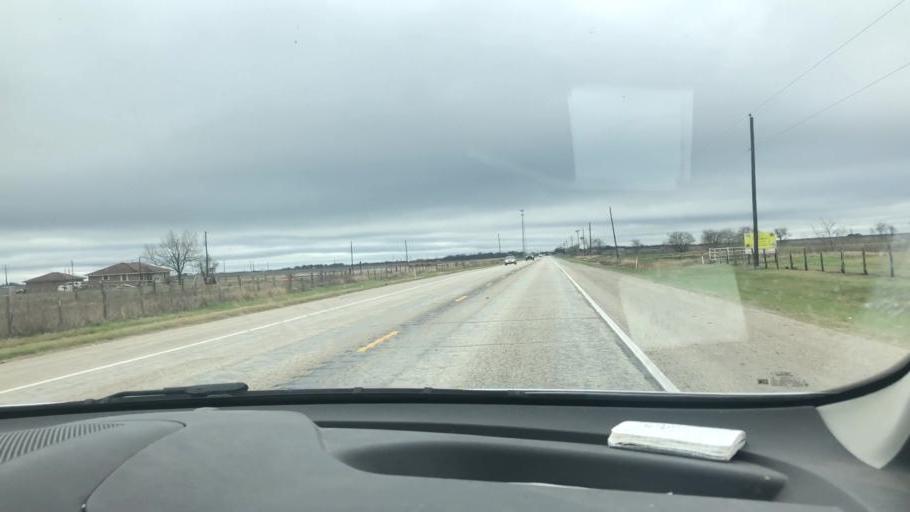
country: US
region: Texas
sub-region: Wharton County
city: Wharton
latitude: 29.2398
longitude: -96.0415
